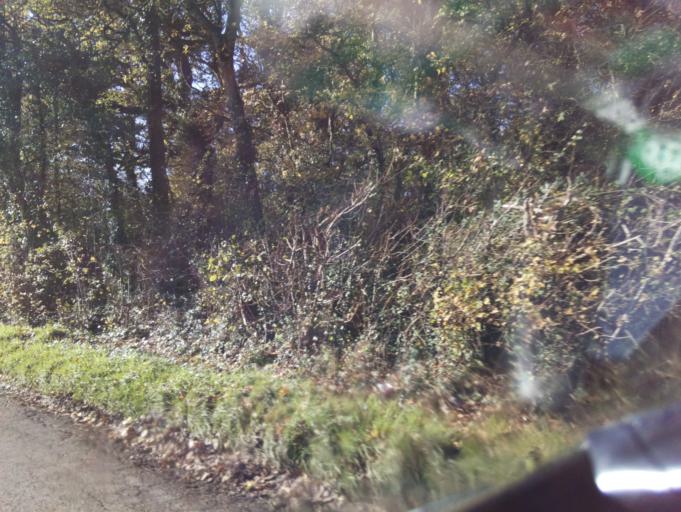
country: GB
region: England
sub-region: Somerset
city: Yeovil
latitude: 50.8842
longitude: -2.5884
